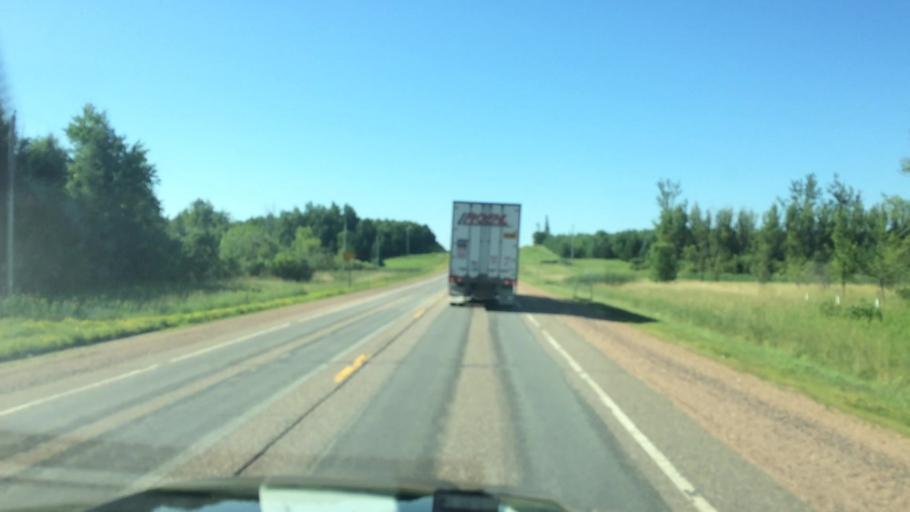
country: US
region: Wisconsin
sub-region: Marathon County
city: Athens
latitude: 44.9289
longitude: -90.0789
